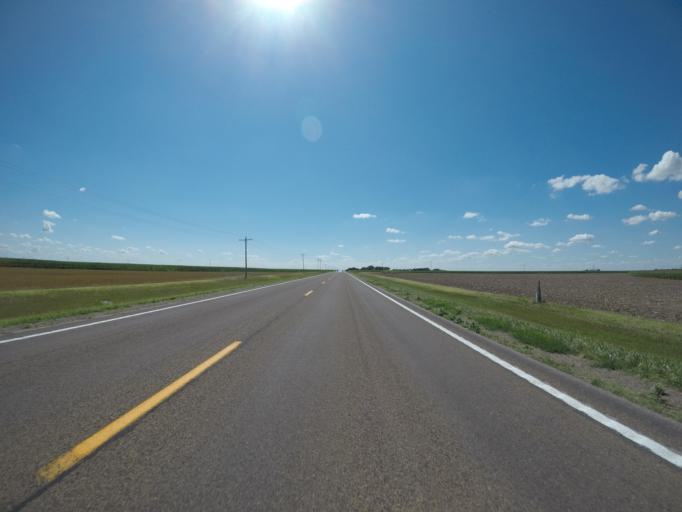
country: US
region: Nebraska
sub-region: Chase County
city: Imperial
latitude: 40.5376
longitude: -101.7967
